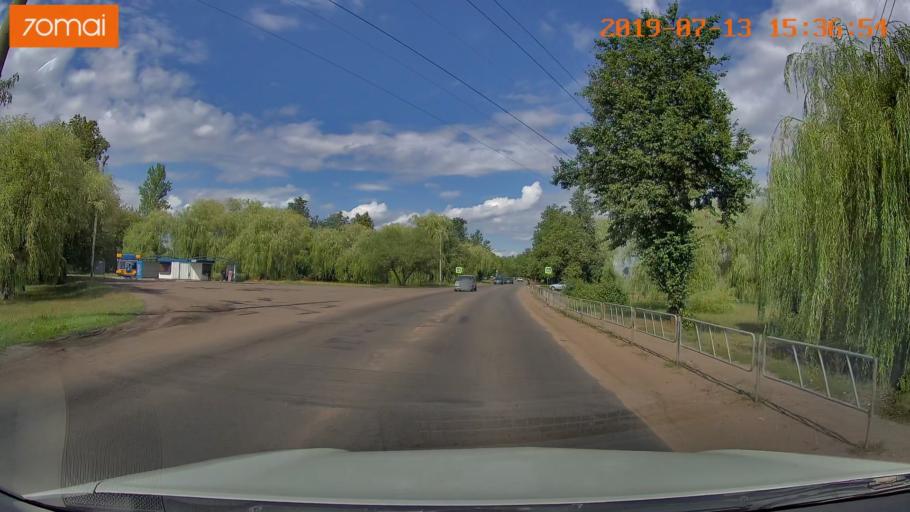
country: BY
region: Mogilev
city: Babruysk
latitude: 53.1350
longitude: 29.1670
